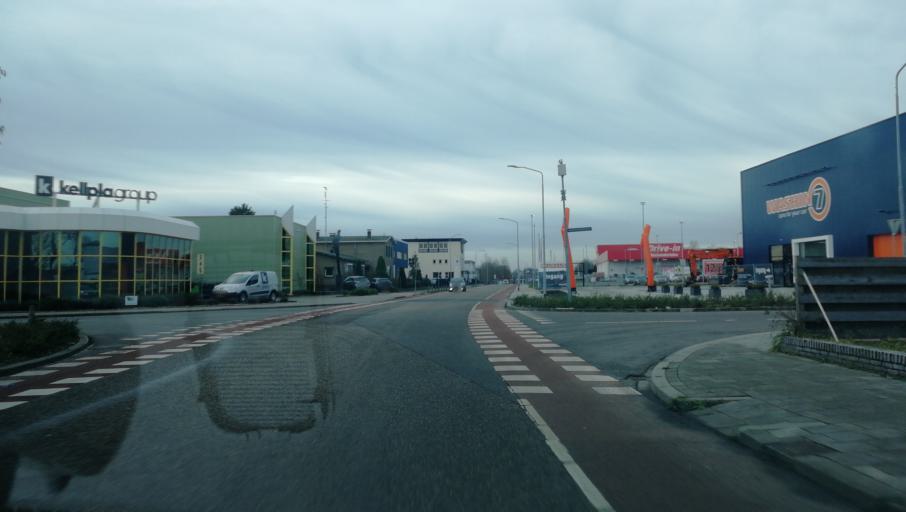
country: NL
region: Limburg
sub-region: Gemeente Venlo
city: Venlo
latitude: 51.3886
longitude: 6.1816
